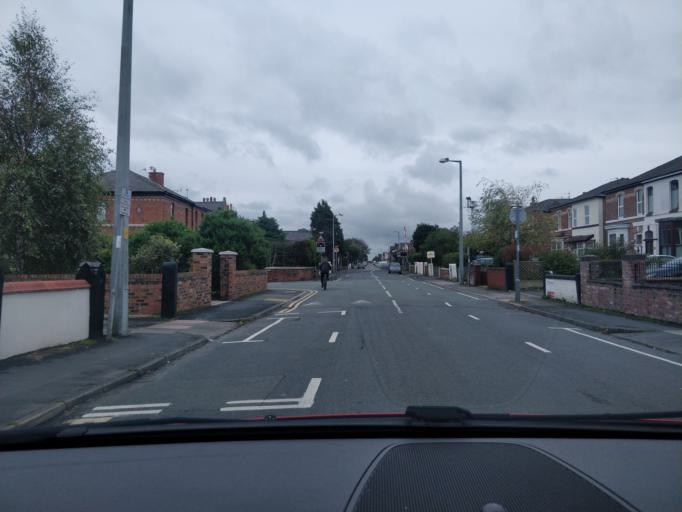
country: GB
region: England
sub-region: Sefton
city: Southport
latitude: 53.6422
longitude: -3.0046
